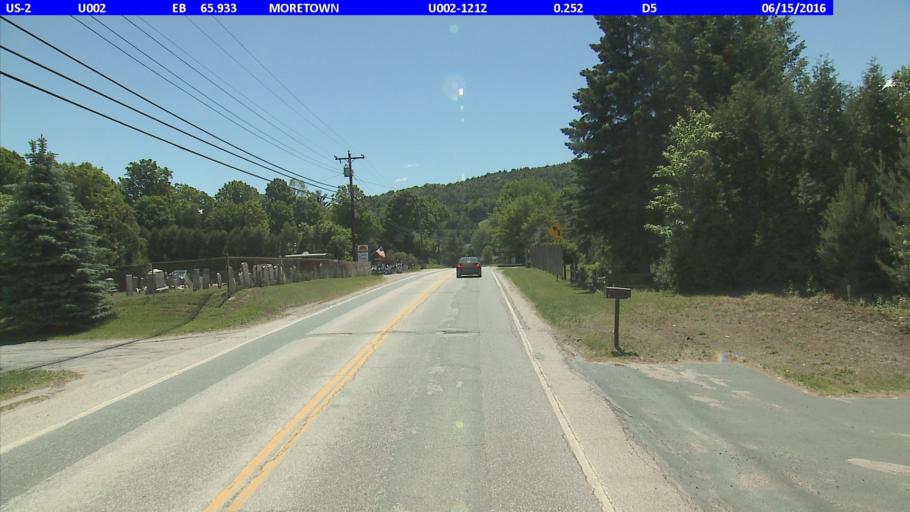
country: US
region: Vermont
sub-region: Washington County
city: Waterbury
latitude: 44.3241
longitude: -72.7430
